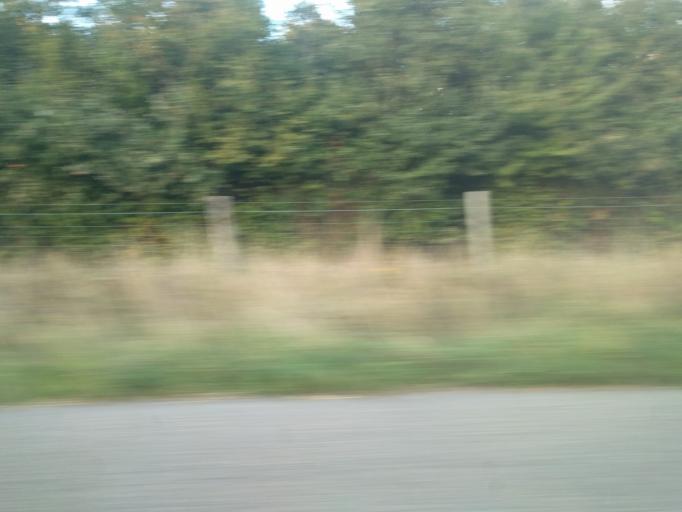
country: DK
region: South Denmark
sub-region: Nyborg Kommune
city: Nyborg
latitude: 55.3375
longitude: 10.7249
